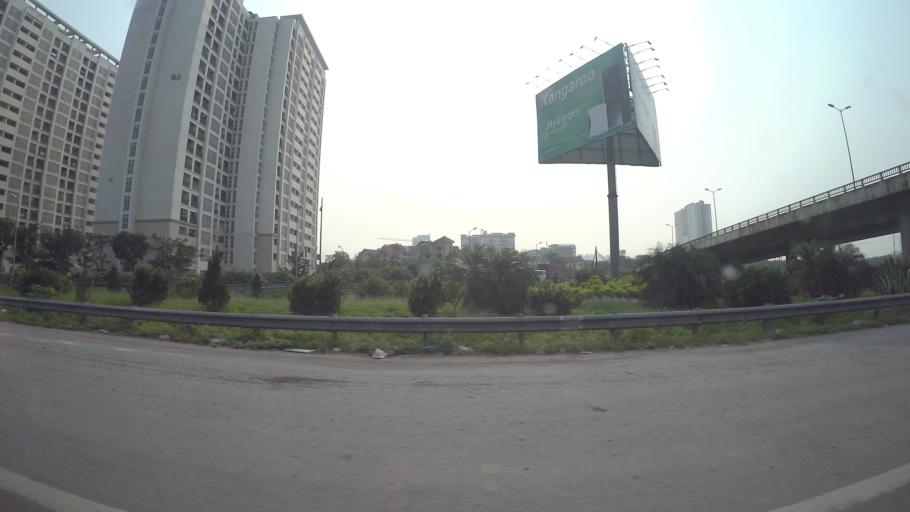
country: VN
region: Ha Noi
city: Van Dien
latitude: 20.9605
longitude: 105.8491
